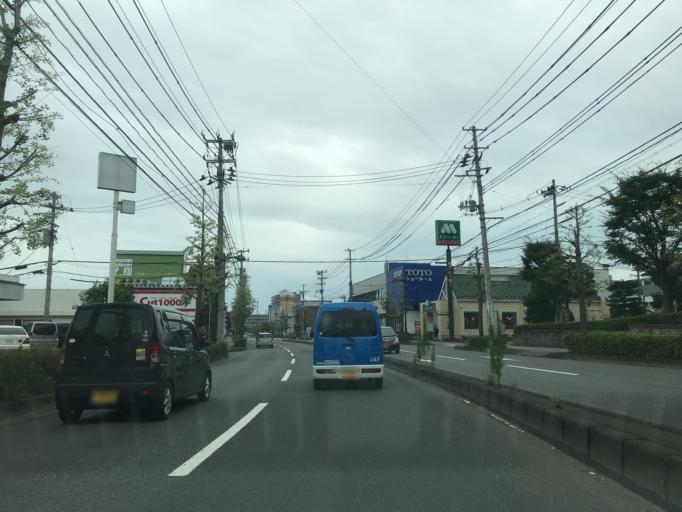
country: JP
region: Miyagi
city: Sendai-shi
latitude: 38.3107
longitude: 140.8897
